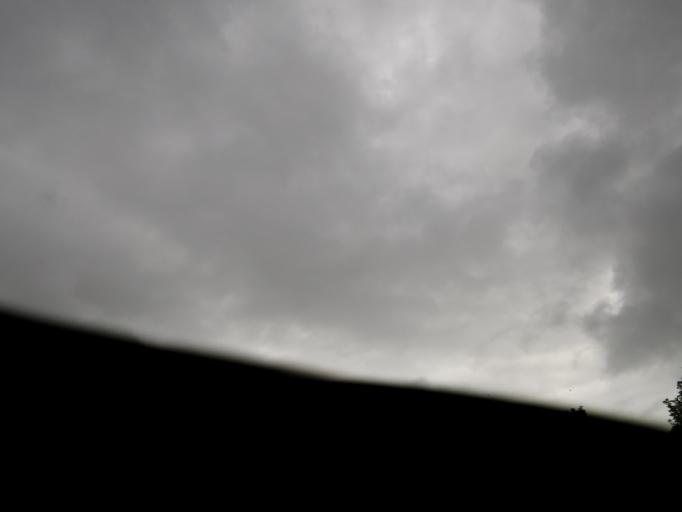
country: US
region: Illinois
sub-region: Jefferson County
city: Mount Vernon
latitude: 38.3456
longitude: -88.9762
